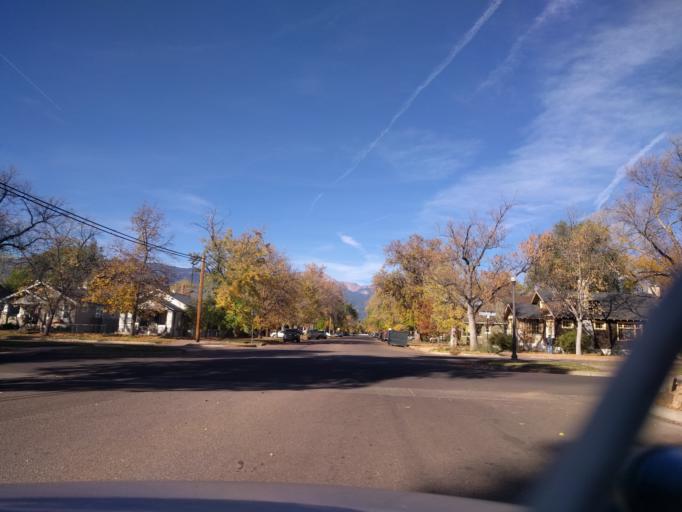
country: US
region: Colorado
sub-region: El Paso County
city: Colorado Springs
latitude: 38.8519
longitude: -104.8167
